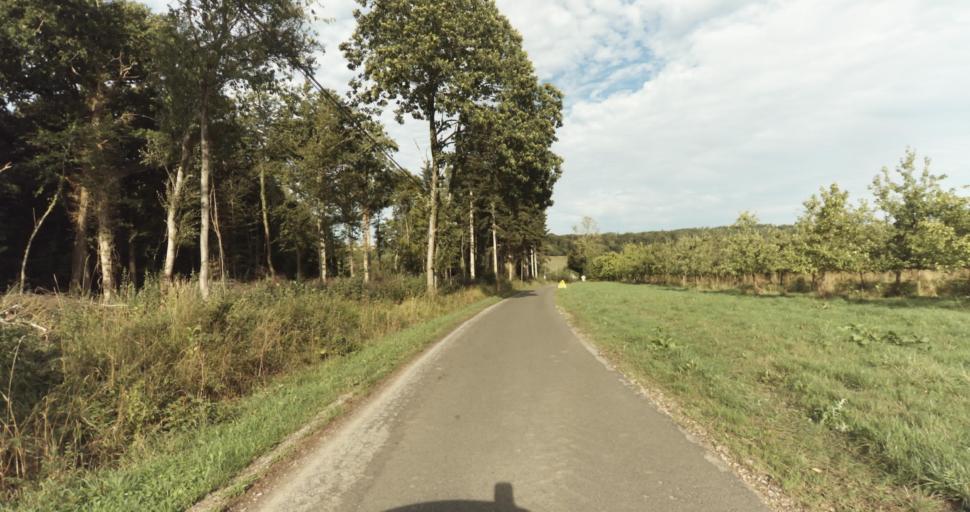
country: FR
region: Lower Normandy
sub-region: Departement de l'Orne
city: Gace
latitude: 48.8263
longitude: 0.2267
